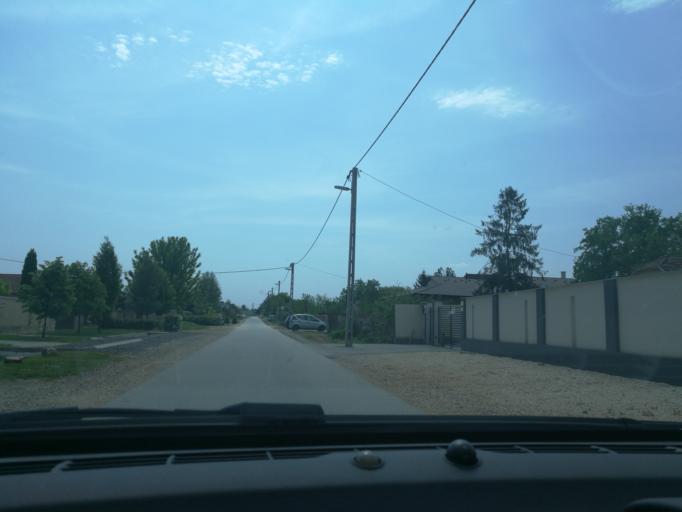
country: HU
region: Szabolcs-Szatmar-Bereg
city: Nyiregyhaza
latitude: 47.9620
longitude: 21.6849
